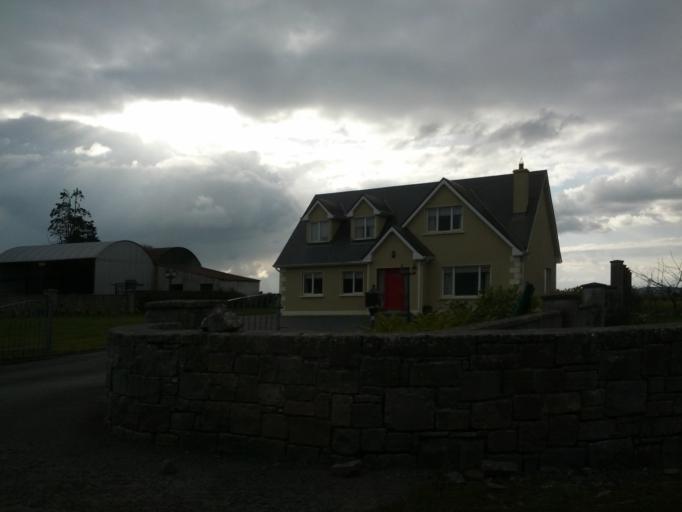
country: IE
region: Connaught
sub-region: County Galway
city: Athenry
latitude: 53.4231
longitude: -8.6155
